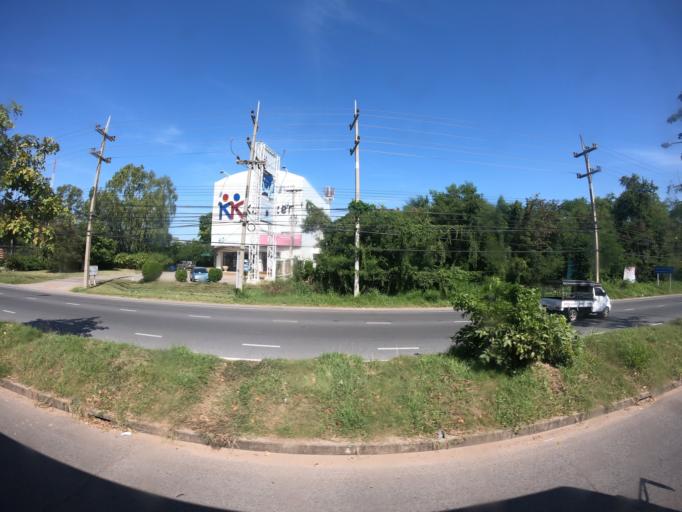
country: TH
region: Nakhon Ratchasima
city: Nakhon Ratchasima
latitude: 14.9982
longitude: 102.1147
